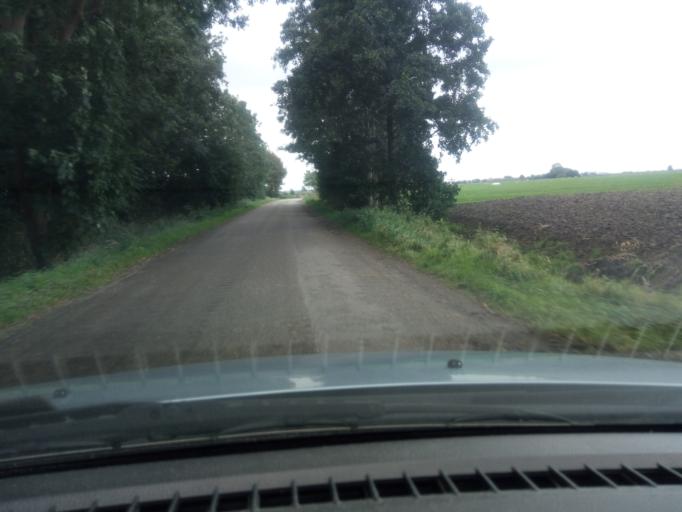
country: NL
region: Groningen
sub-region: Gemeente Grootegast
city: Grootegast
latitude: 53.2634
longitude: 6.2482
